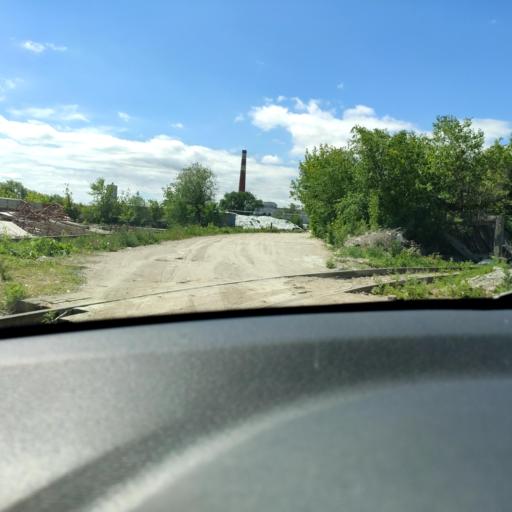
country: RU
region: Samara
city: Samara
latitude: 53.1780
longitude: 50.2112
